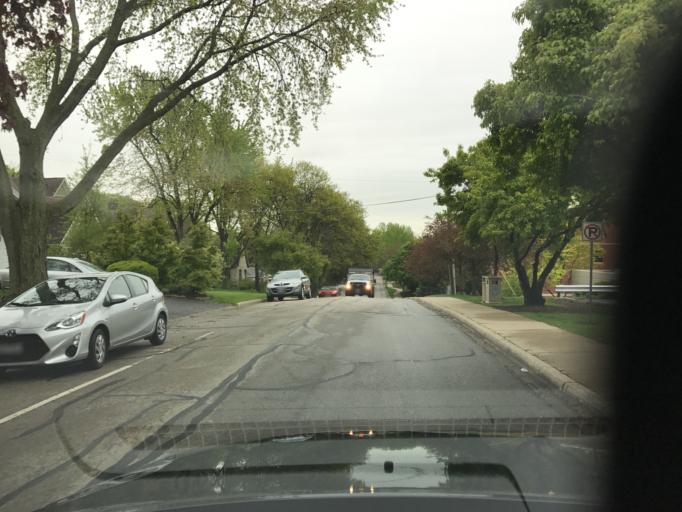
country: US
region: Illinois
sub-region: DuPage County
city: Naperville
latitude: 41.7711
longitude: -88.1421
